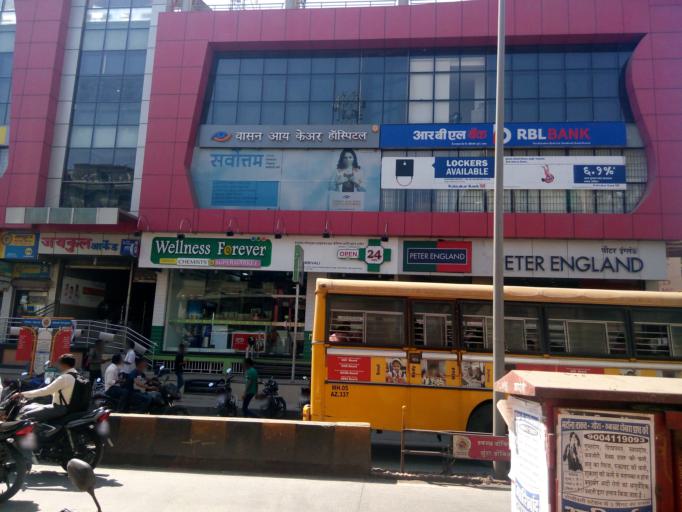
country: IN
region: Maharashtra
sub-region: Thane
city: Dombivli
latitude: 19.2101
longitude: 73.0934
